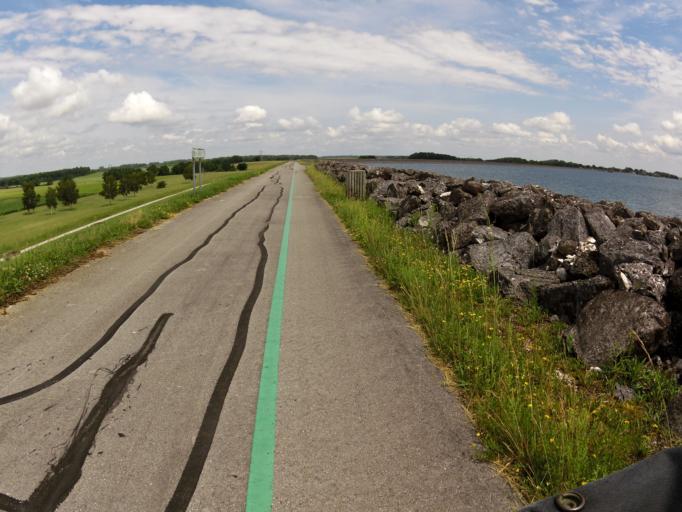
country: FR
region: Champagne-Ardenne
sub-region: Departement de l'Aube
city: Brienne-le-Chateau
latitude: 48.3446
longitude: 4.4383
